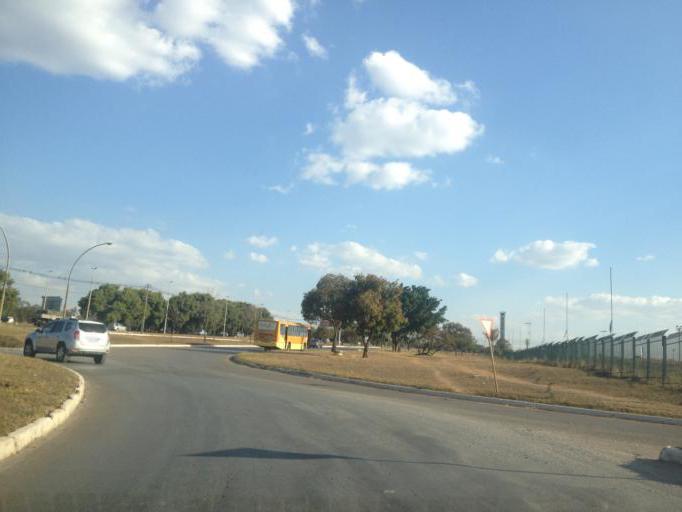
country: BR
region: Federal District
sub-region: Brasilia
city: Brasilia
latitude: -15.7517
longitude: -47.9252
